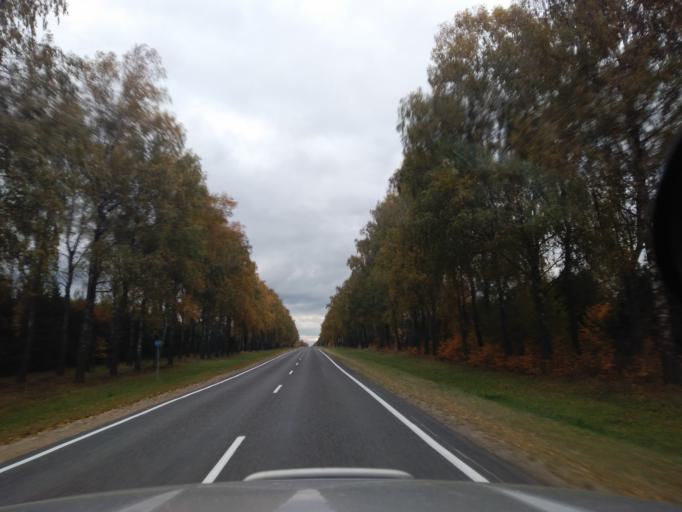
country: BY
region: Minsk
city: Slutsk
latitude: 53.2215
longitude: 27.5011
